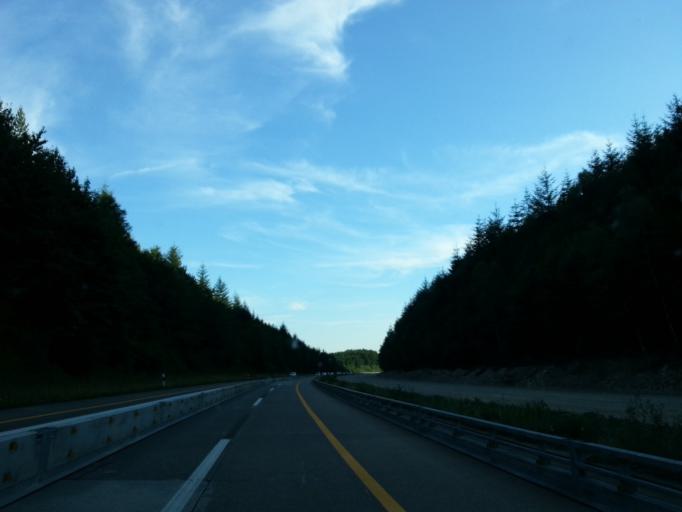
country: DE
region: Rheinland-Pfalz
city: Hinzert-Polert
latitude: 49.7133
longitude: 6.8942
